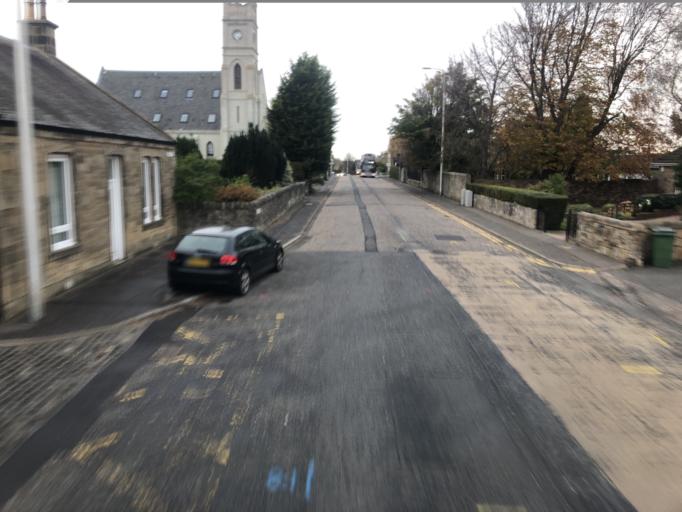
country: GB
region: Scotland
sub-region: Midlothian
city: Loanhead
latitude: 55.8796
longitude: -3.1507
